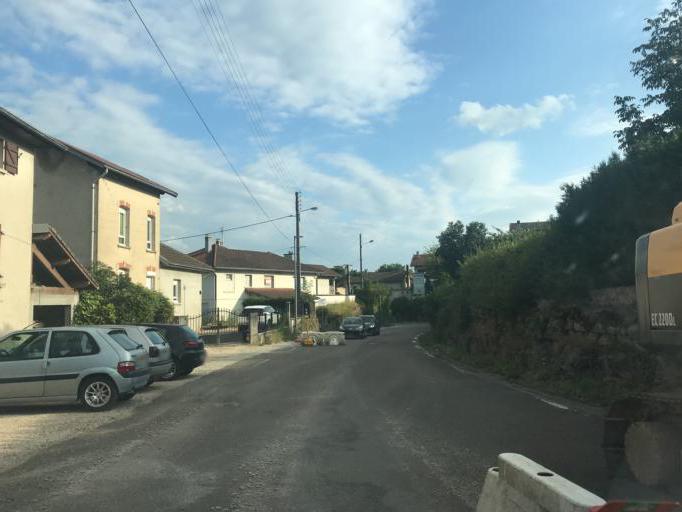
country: FR
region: Franche-Comte
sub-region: Departement du Jura
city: Lavans-les-Saint-Claude
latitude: 46.3877
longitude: 5.7854
